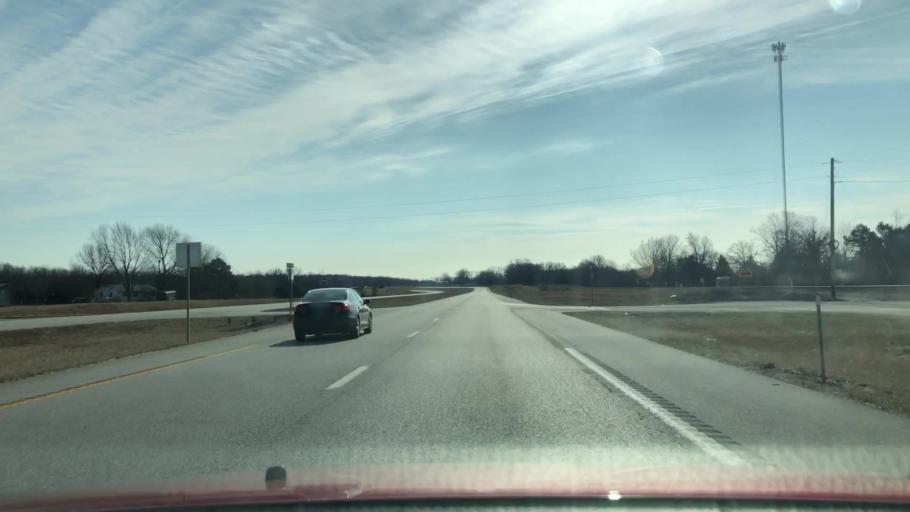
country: US
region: Missouri
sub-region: Webster County
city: Seymour
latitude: 37.1389
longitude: -92.7450
